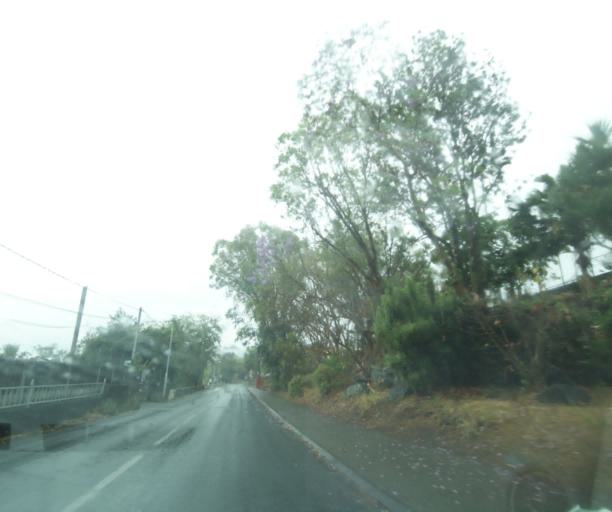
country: RE
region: Reunion
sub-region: Reunion
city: Saint-Paul
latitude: -21.0179
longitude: 55.3029
